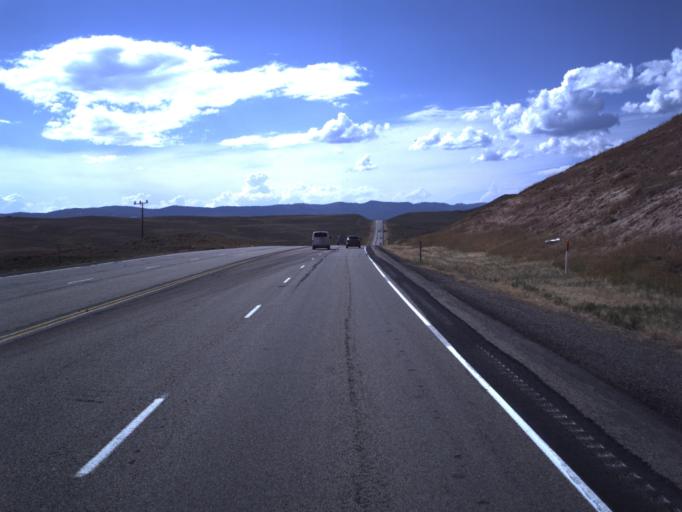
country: US
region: Utah
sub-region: Wasatch County
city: Heber
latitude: 40.1845
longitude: -111.0580
